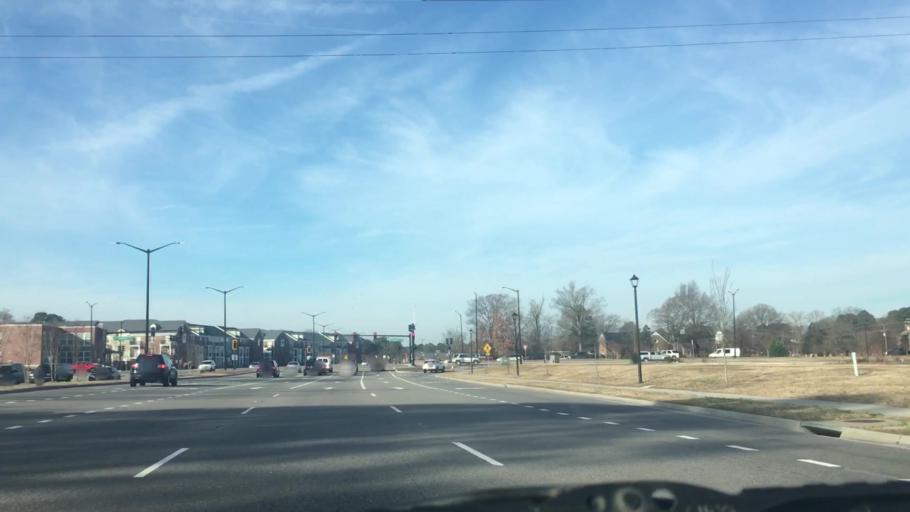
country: US
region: Virginia
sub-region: City of Chesapeake
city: Chesapeake
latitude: 36.8253
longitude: -76.1592
